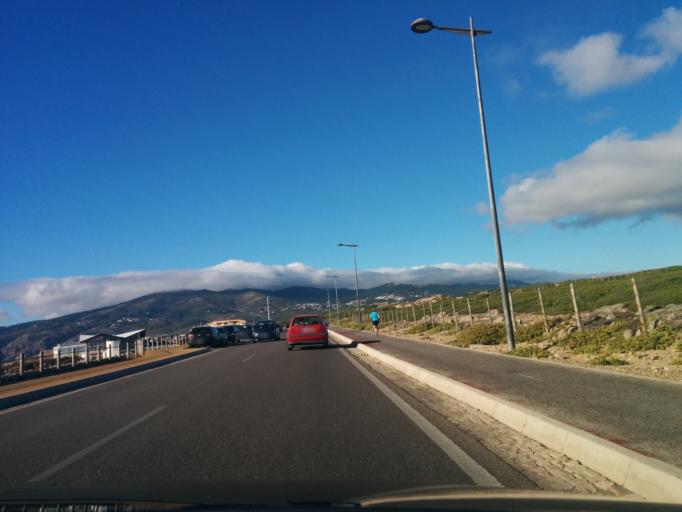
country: PT
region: Lisbon
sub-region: Cascais
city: Cascais
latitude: 38.7194
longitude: -9.4789
